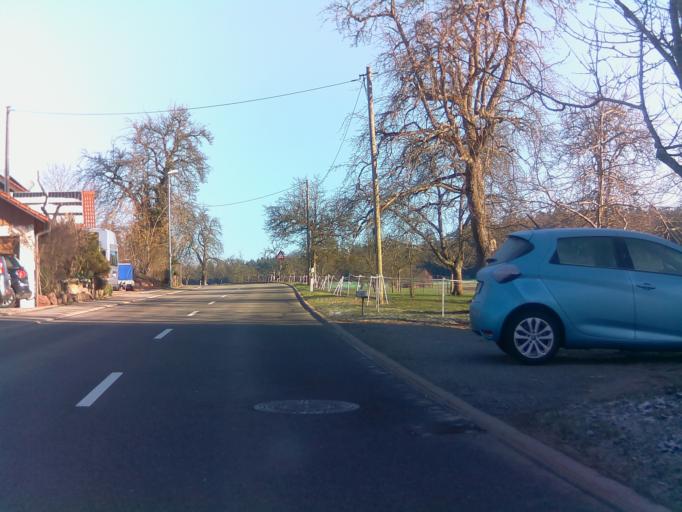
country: DE
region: Baden-Wuerttemberg
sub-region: Karlsruhe Region
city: Neuweiler
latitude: 48.6962
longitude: 8.5914
